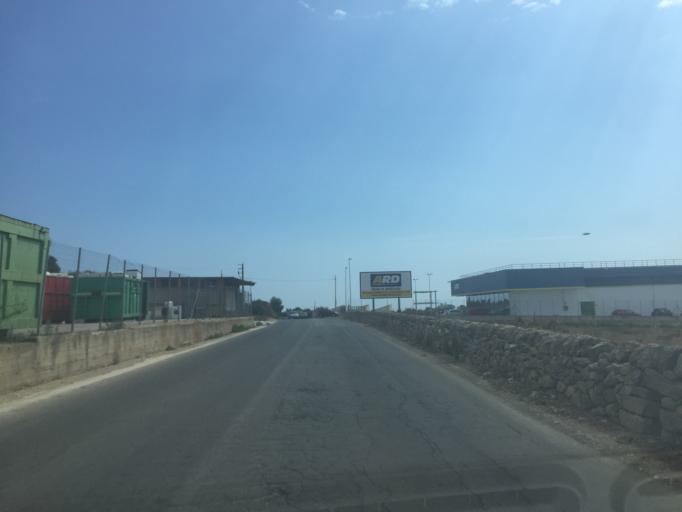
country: IT
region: Sicily
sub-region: Ragusa
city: Santa Croce Camerina
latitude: 36.8266
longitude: 14.5190
